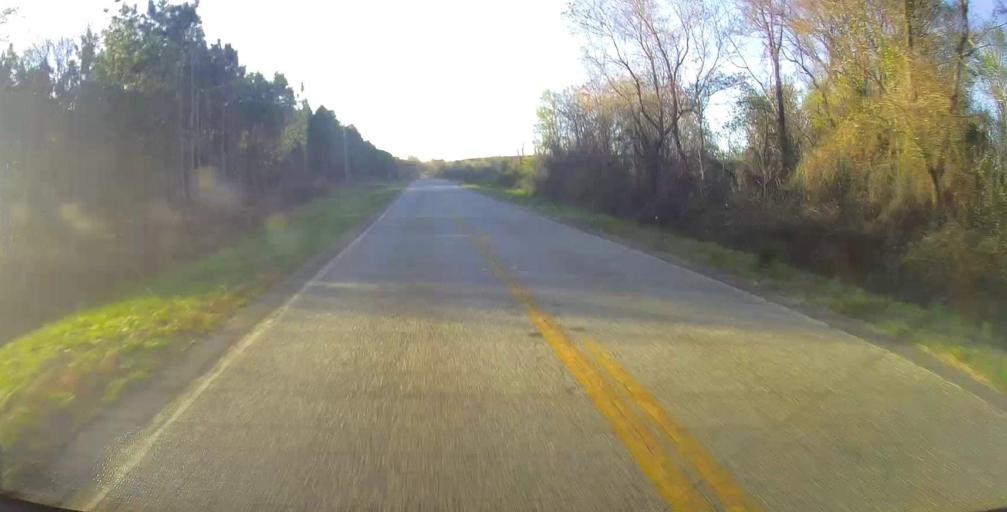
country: US
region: Georgia
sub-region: Wilcox County
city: Abbeville
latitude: 32.1139
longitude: -83.3208
